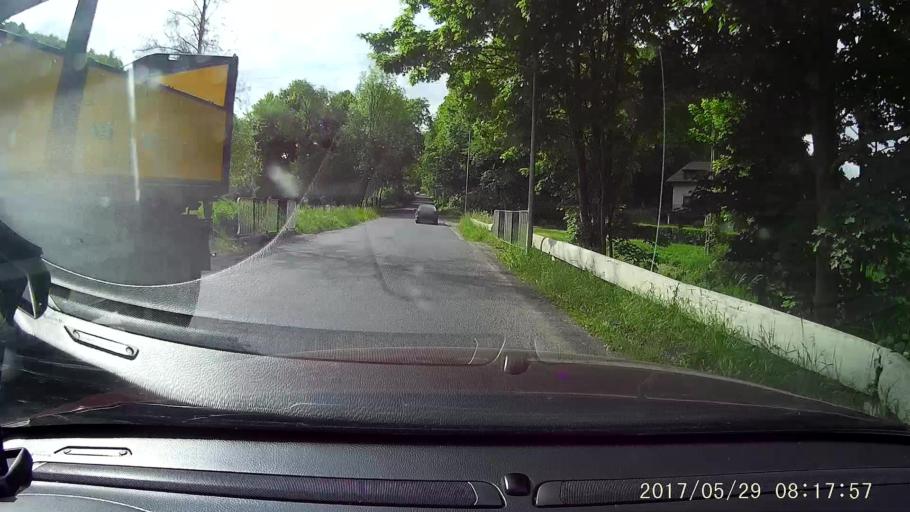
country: PL
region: Lower Silesian Voivodeship
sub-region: Powiat zlotoryjski
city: Zlotoryja
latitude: 51.1114
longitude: 15.8898
